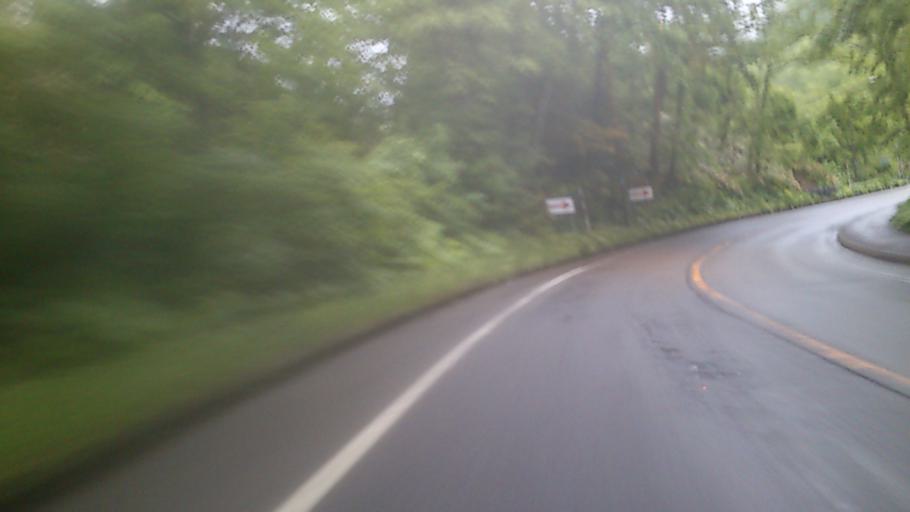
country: JP
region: Hokkaido
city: Shiraoi
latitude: 42.7674
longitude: 141.4150
